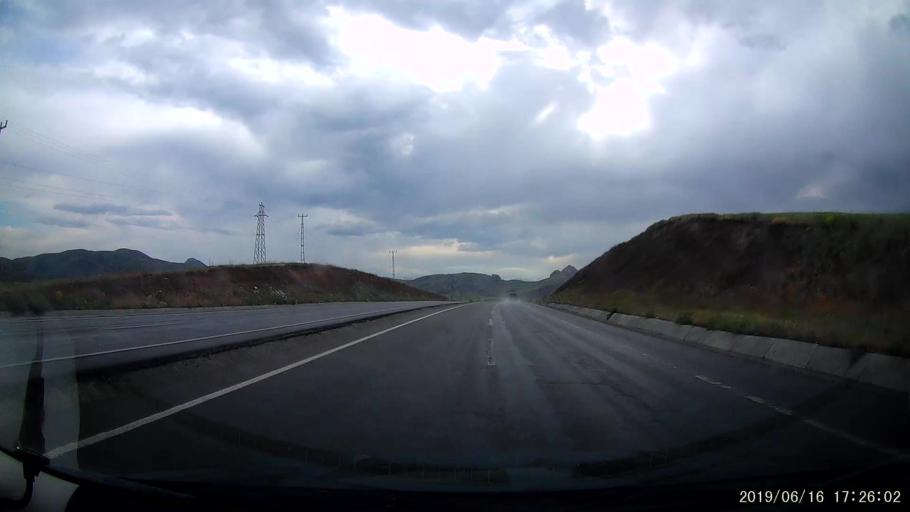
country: TR
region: Erzincan
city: Tercan
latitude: 39.7664
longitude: 40.4212
